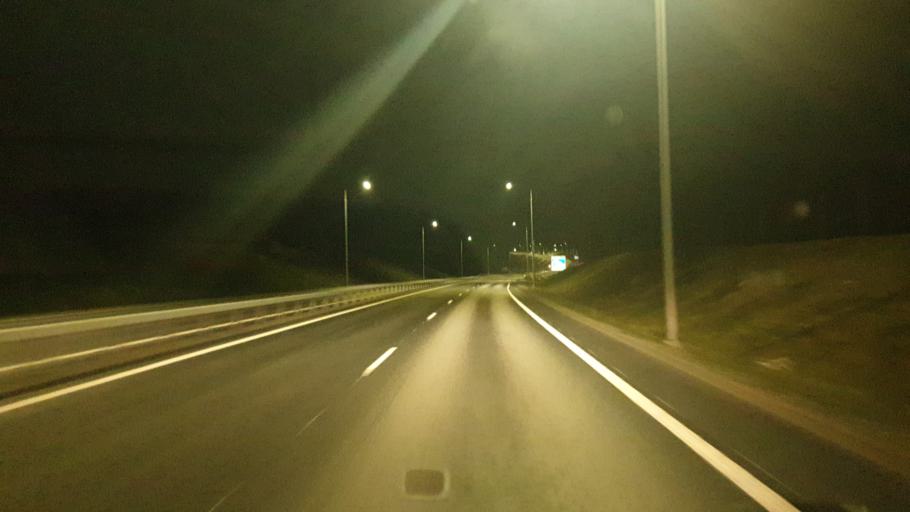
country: FI
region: Central Finland
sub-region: AEaenekoski
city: AEaenekoski
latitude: 62.5995
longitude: 25.6895
